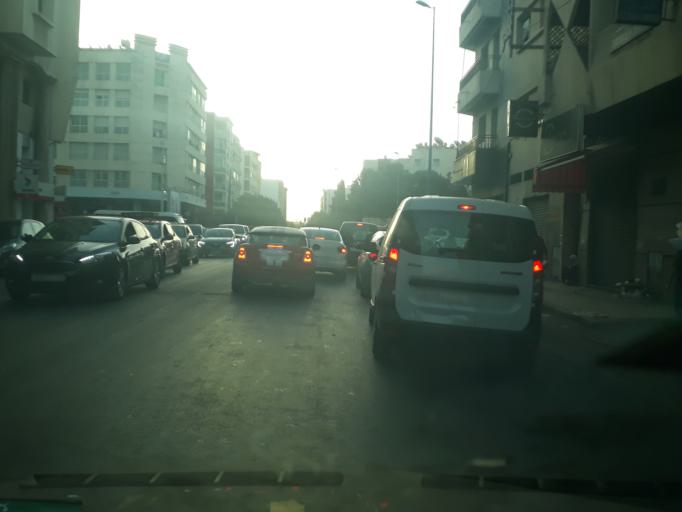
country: MA
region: Grand Casablanca
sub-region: Casablanca
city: Casablanca
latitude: 33.5739
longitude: -7.6414
